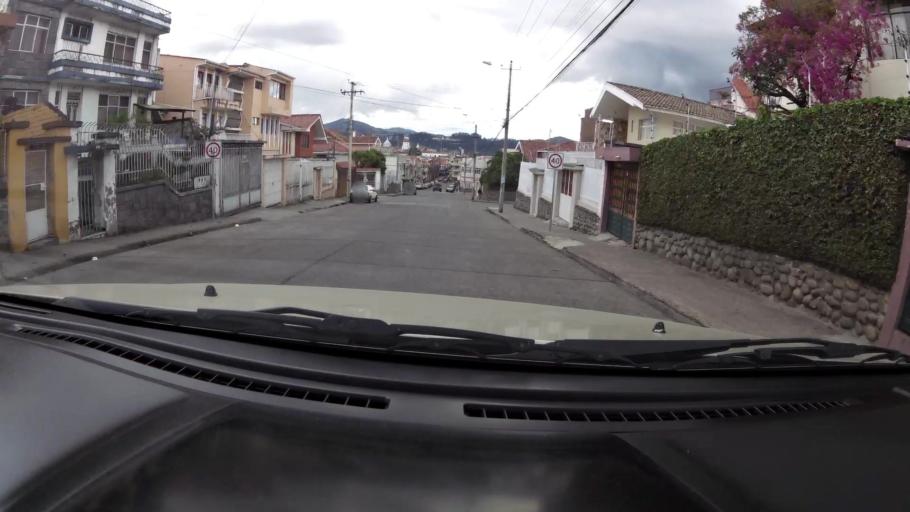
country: EC
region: Azuay
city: Cuenca
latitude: -2.8896
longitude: -79.0056
